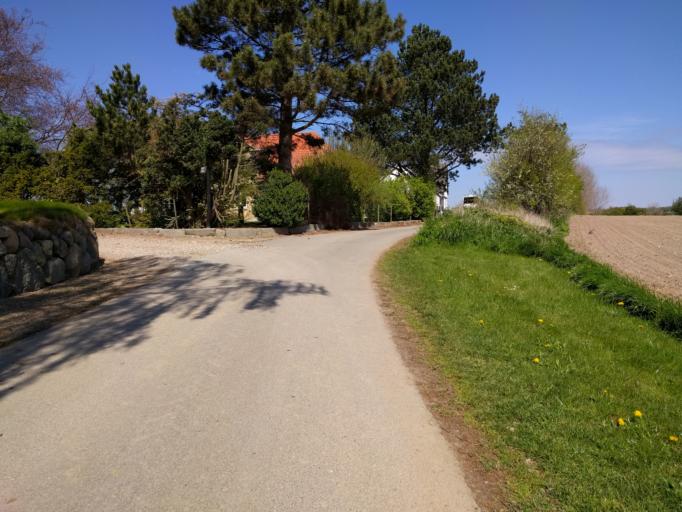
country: DK
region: South Denmark
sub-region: Kerteminde Kommune
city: Munkebo
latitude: 55.4519
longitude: 10.5897
